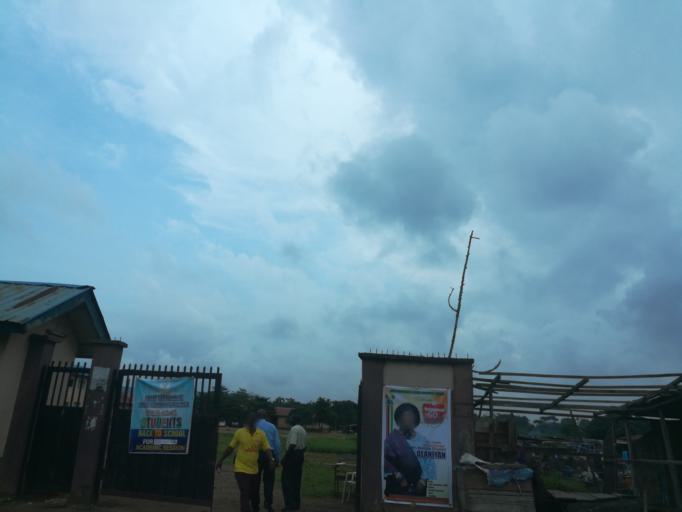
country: NG
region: Lagos
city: Oshodi
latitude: 6.5636
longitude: 3.3520
